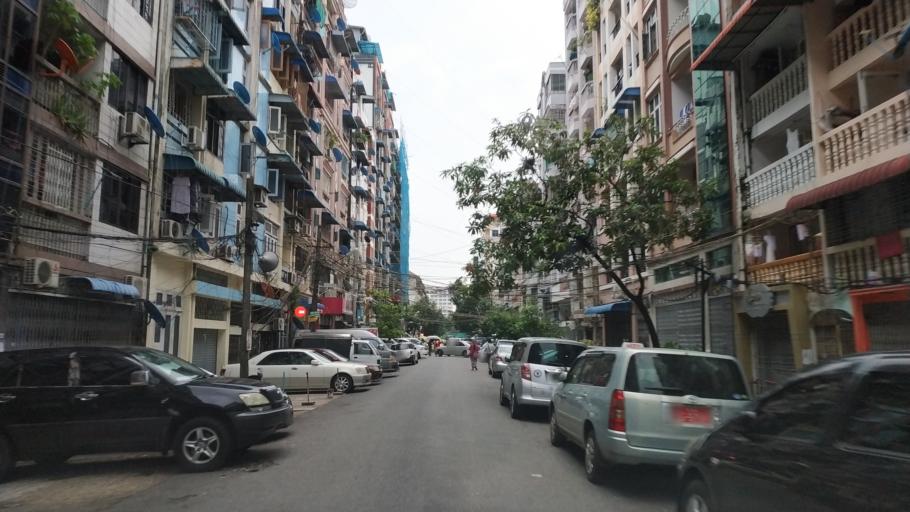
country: MM
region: Yangon
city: Yangon
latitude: 16.7779
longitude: 96.1689
